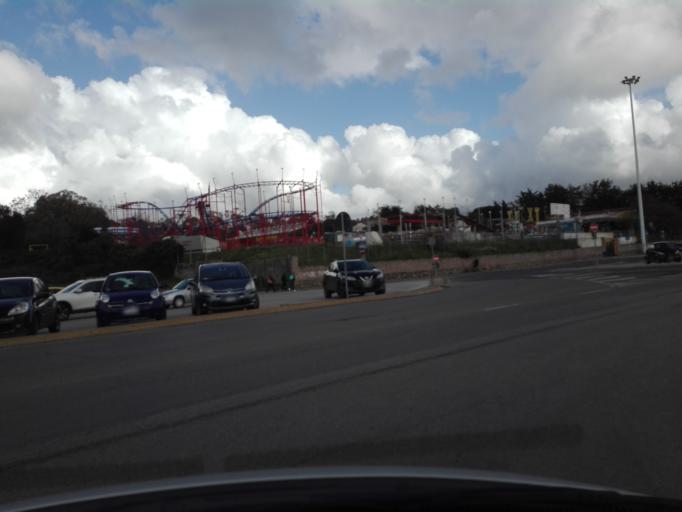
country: IT
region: Sardinia
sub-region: Provincia di Sassari
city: Sassari
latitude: 40.7191
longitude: 8.5819
